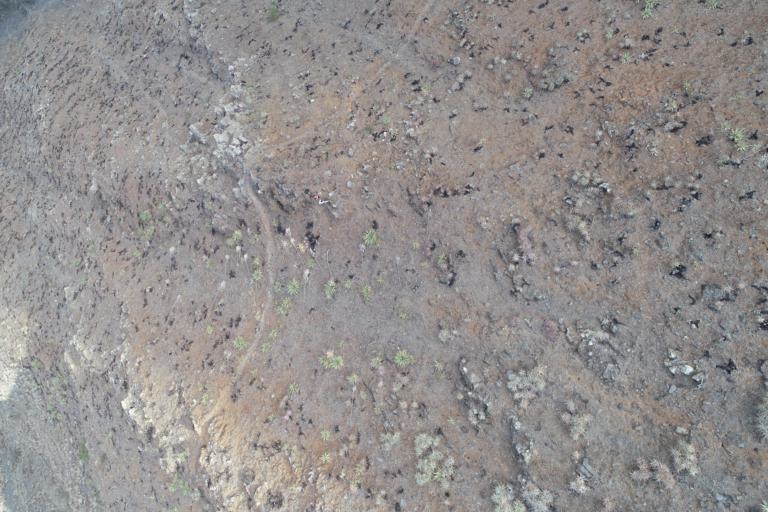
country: BO
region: La Paz
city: Sorata
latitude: -15.5205
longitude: -68.6905
